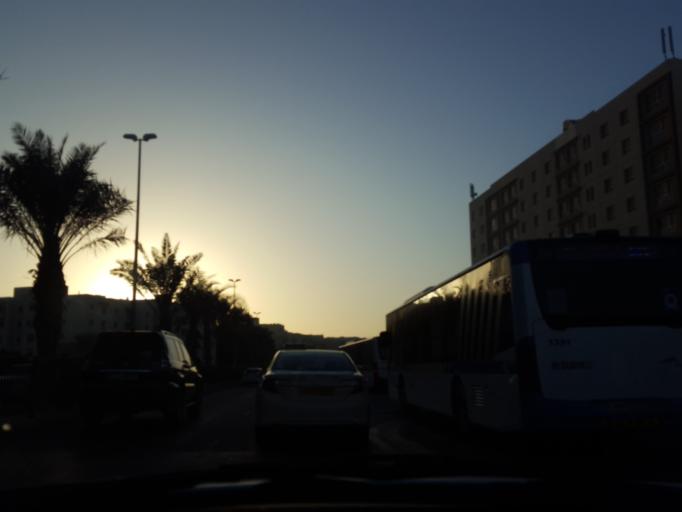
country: AE
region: Dubai
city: Dubai
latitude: 25.1427
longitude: 55.2514
